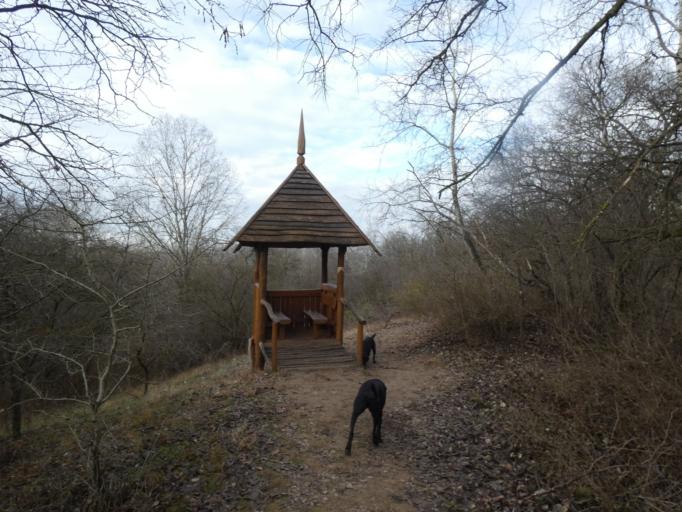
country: HU
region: Pest
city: Kakucs
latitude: 47.2825
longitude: 19.4127
